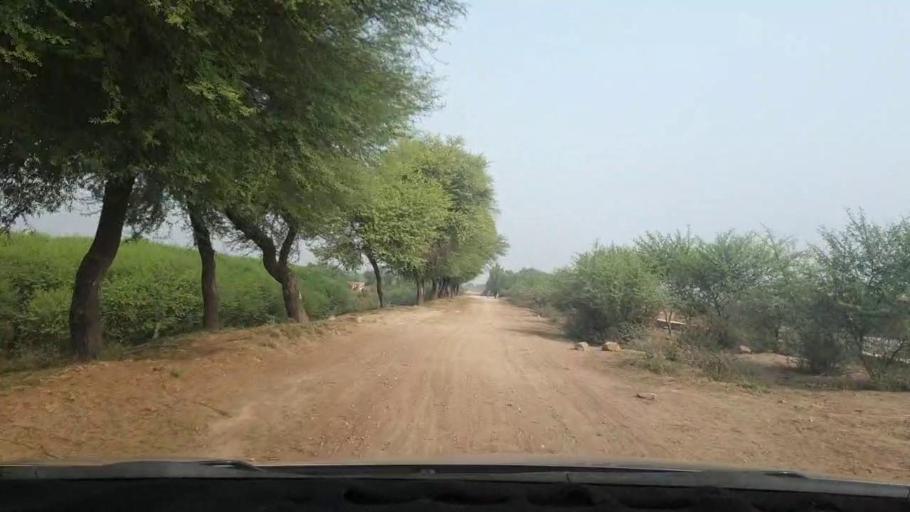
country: PK
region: Sindh
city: Matiari
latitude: 25.6473
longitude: 68.5607
